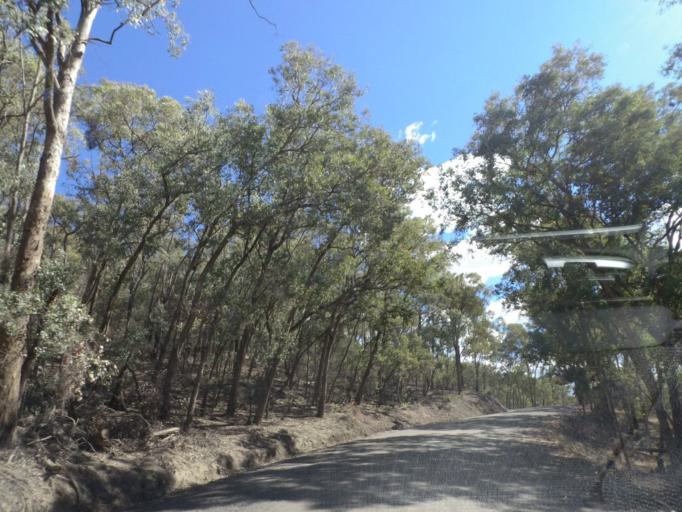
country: AU
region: Victoria
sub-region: Murrindindi
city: Alexandra
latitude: -37.3158
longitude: 145.8167
